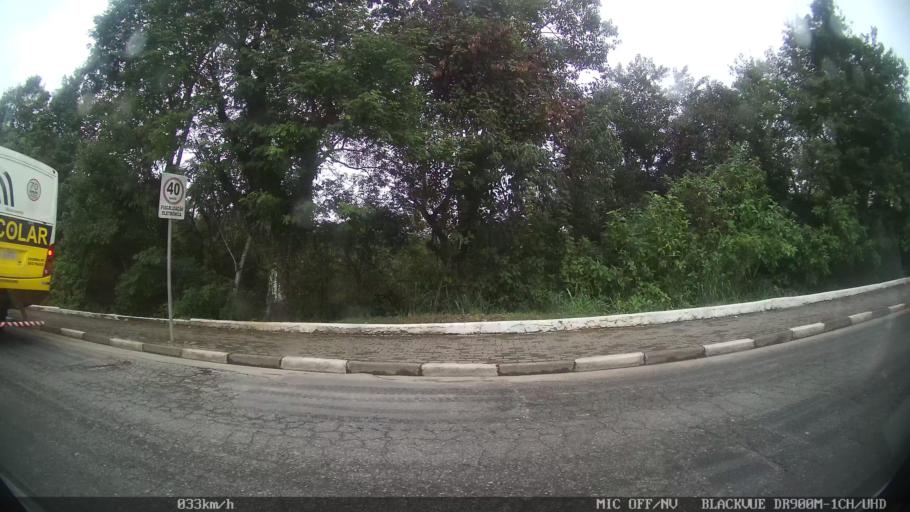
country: BR
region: Sao Paulo
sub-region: Juquia
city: Juquia
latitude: -24.3239
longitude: -47.6349
